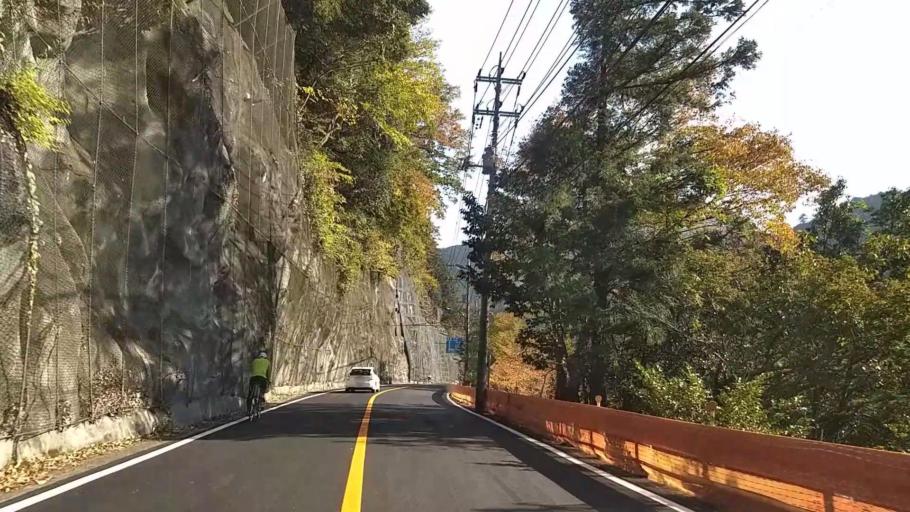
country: JP
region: Tokyo
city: Ome
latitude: 35.8151
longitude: 139.1320
